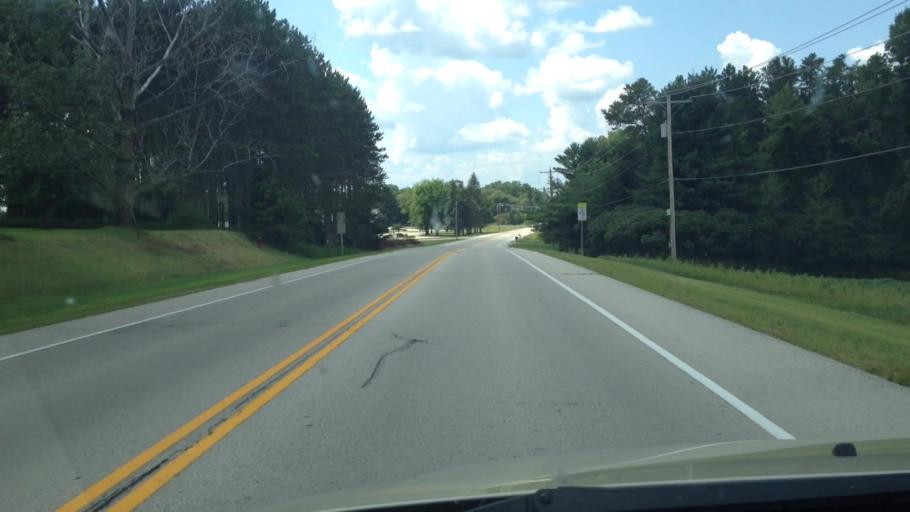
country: US
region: Wisconsin
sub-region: Brown County
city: Suamico
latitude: 44.6366
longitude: -88.0638
